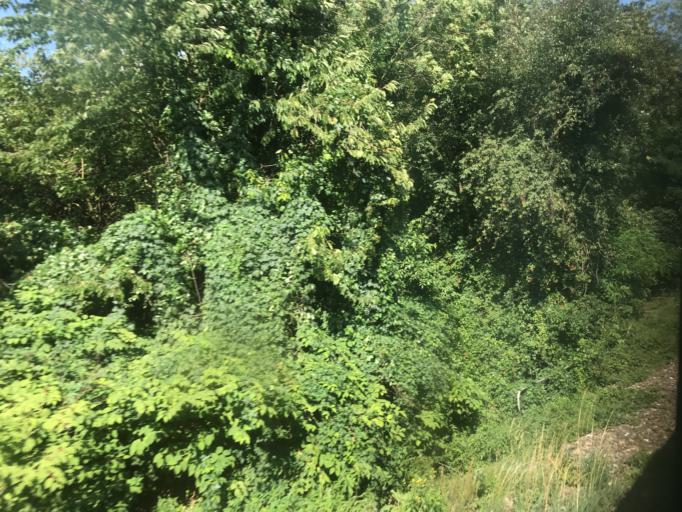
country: AT
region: Upper Austria
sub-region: Politischer Bezirk Linz-Land
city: Asten
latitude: 48.2608
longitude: 14.4176
